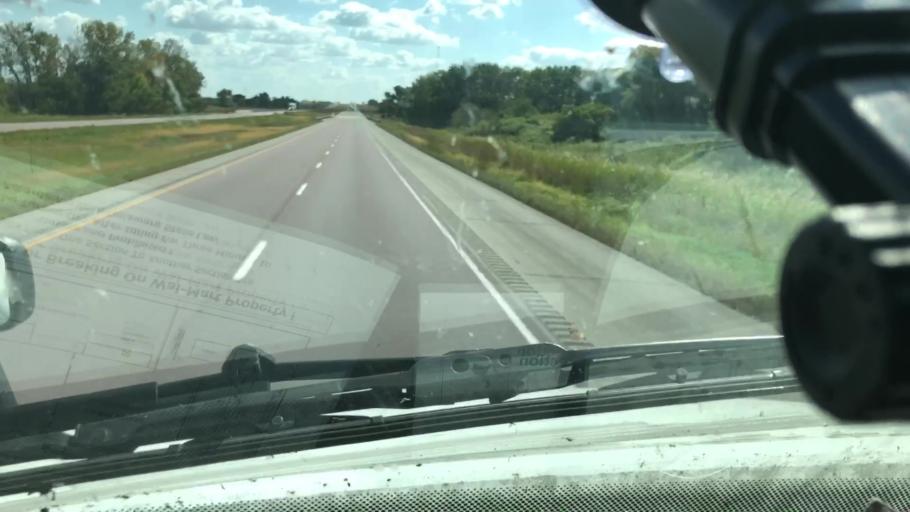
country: US
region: Iowa
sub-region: Worth County
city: Northwood
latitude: 43.3926
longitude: -93.3496
